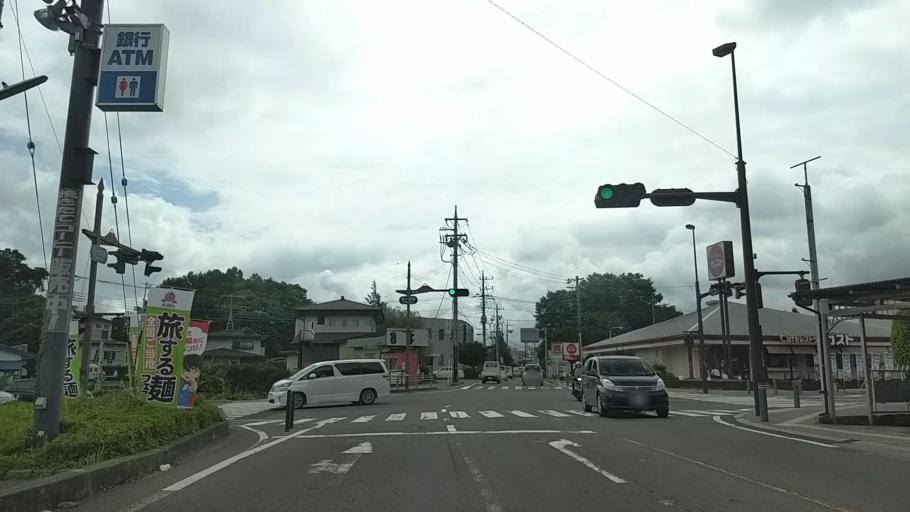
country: JP
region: Yamanashi
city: Fujikawaguchiko
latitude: 35.5033
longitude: 138.7575
